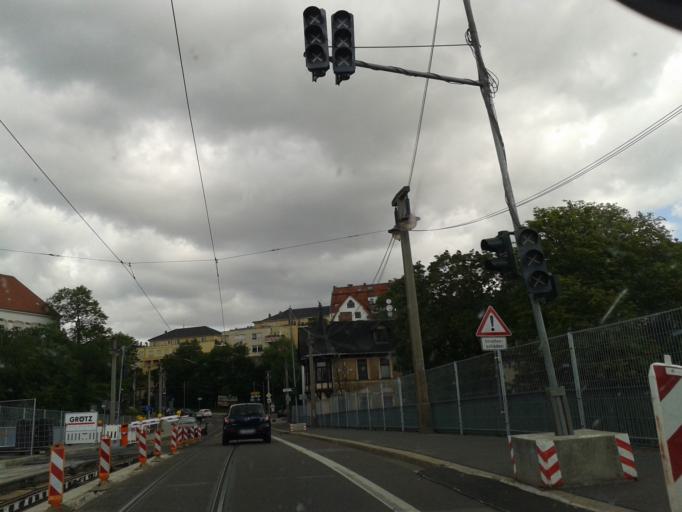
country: DE
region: Saxony-Anhalt
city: Sennewitz
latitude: 51.5040
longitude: 11.9511
